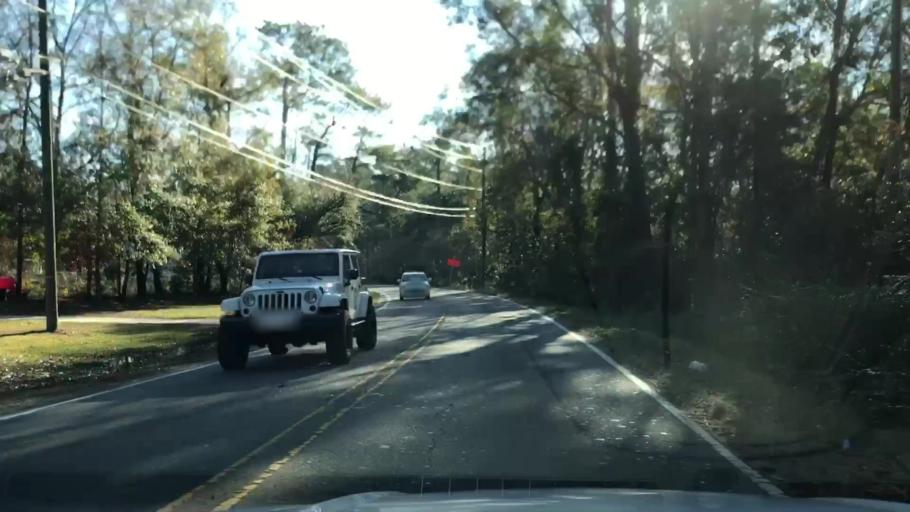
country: US
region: South Carolina
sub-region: Charleston County
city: Lincolnville
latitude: 32.9822
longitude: -80.1400
